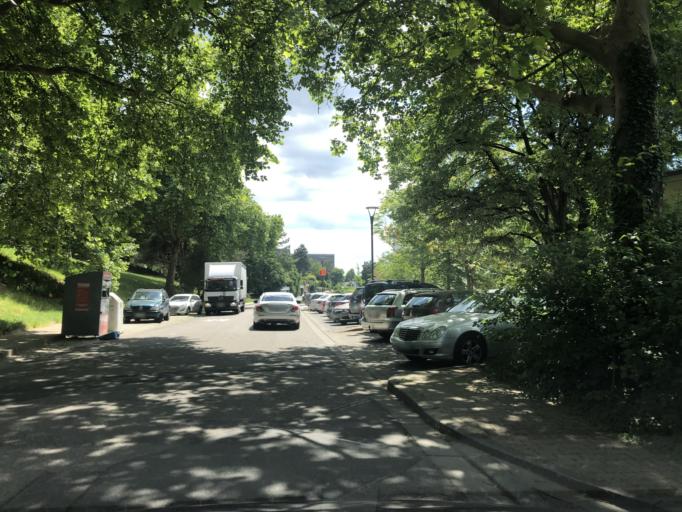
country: DE
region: Baden-Wuerttemberg
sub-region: Karlsruhe Region
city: Heidelberg
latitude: 49.3775
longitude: 8.7041
